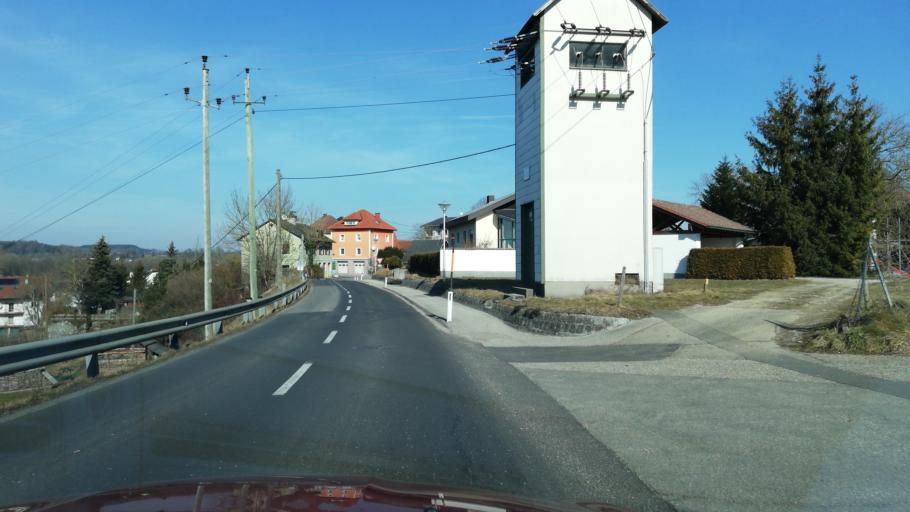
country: AT
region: Upper Austria
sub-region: Politischer Bezirk Vocklabruck
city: Rustorf
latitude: 48.0409
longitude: 13.7898
